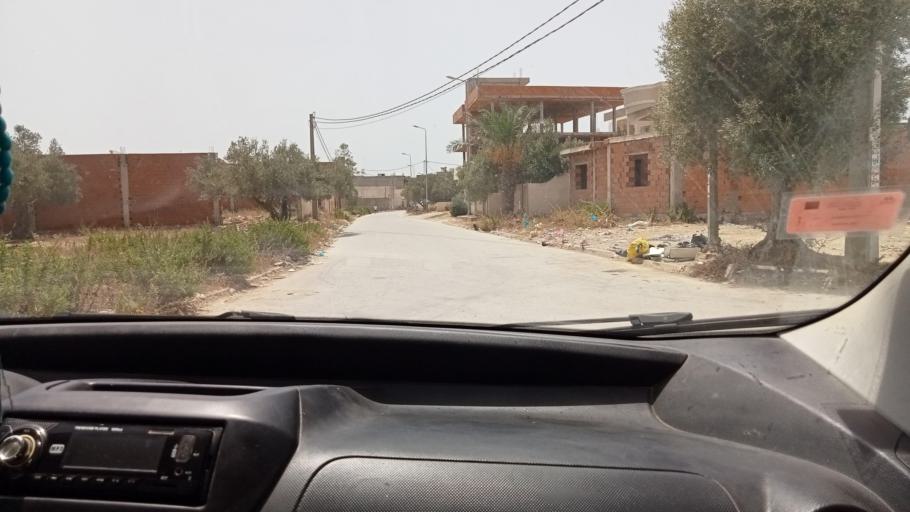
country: TN
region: Nabul
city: Qulaybiyah
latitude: 36.8576
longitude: 11.0866
